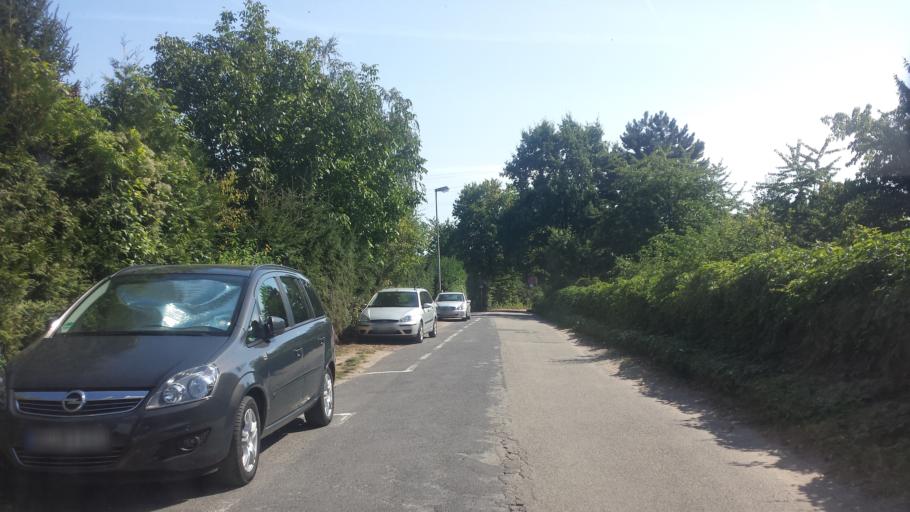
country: DE
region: Rheinland-Pfalz
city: Lachen-Speyerdorf
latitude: 49.3529
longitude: 8.1741
